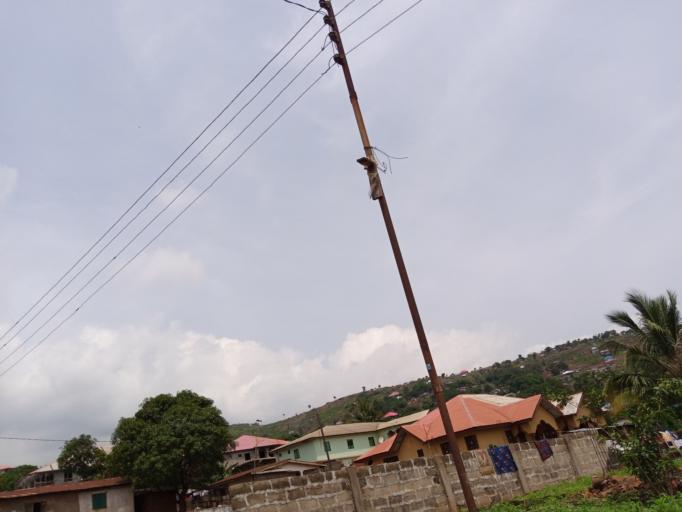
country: SL
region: Western Area
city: Hastings
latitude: 8.3760
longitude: -13.1023
